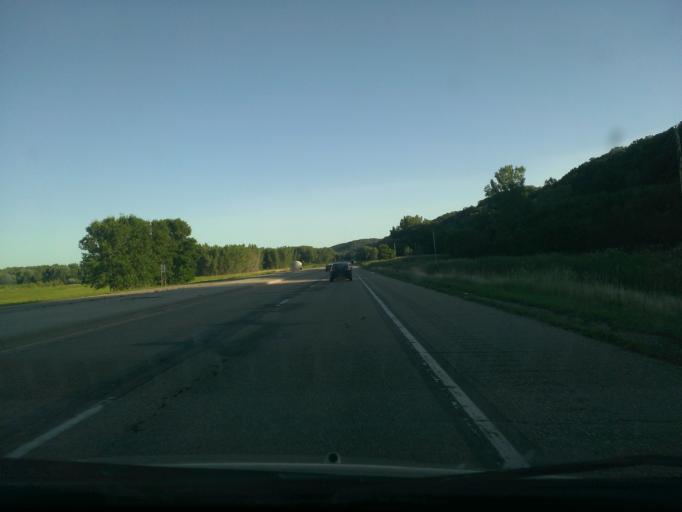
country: US
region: Minnesota
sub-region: Nicollet County
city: North Mankato
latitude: 44.2322
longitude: -94.0273
